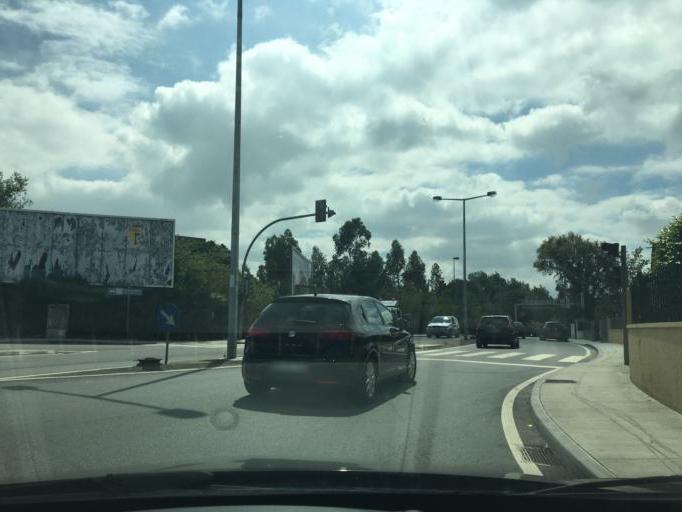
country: PT
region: Porto
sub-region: Maia
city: Gemunde
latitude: 41.2571
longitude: -8.6446
